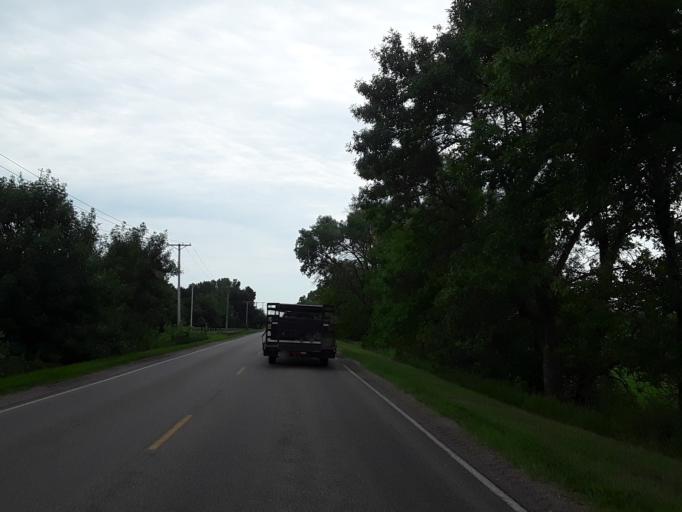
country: US
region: Nebraska
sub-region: Saunders County
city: Yutan
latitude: 41.2382
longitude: -96.3304
